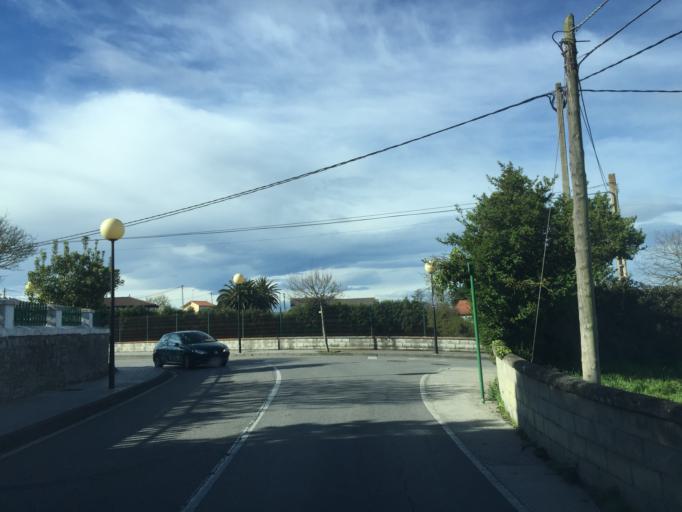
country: ES
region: Asturias
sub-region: Province of Asturias
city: Gijon
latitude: 43.5502
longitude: -5.6162
